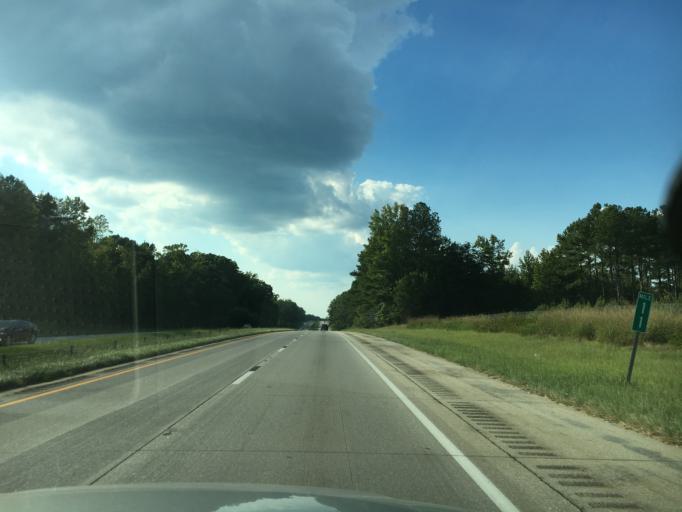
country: US
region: South Carolina
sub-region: Laurens County
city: Watts Mills
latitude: 34.5759
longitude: -82.0365
